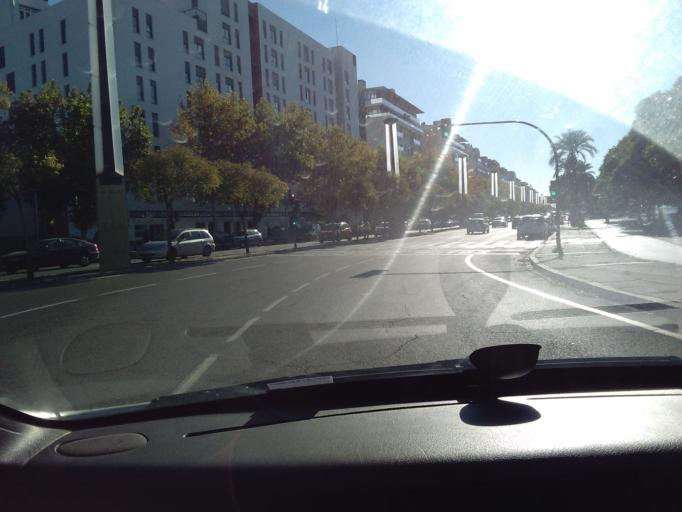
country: ES
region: Andalusia
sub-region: Provincia de Sevilla
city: Sevilla
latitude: 37.4129
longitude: -5.9889
